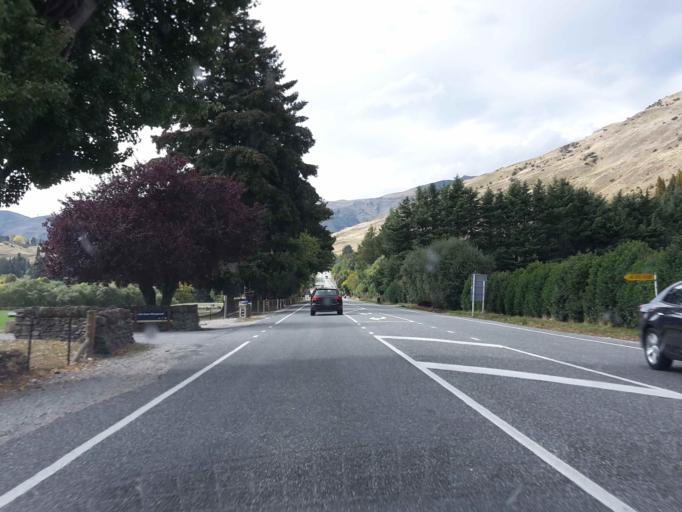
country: NZ
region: Otago
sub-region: Queenstown-Lakes District
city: Arrowtown
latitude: -44.9905
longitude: 168.8095
